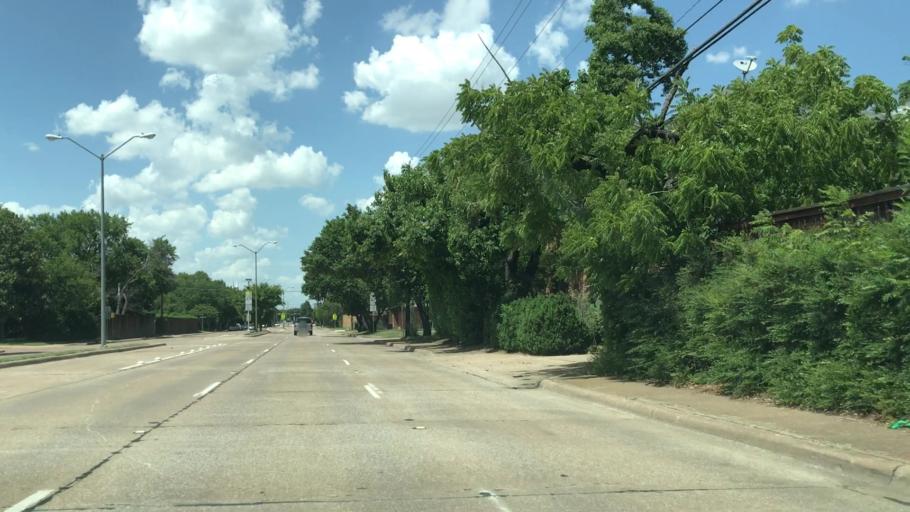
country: US
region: Texas
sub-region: Dallas County
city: University Park
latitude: 32.8761
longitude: -96.8384
